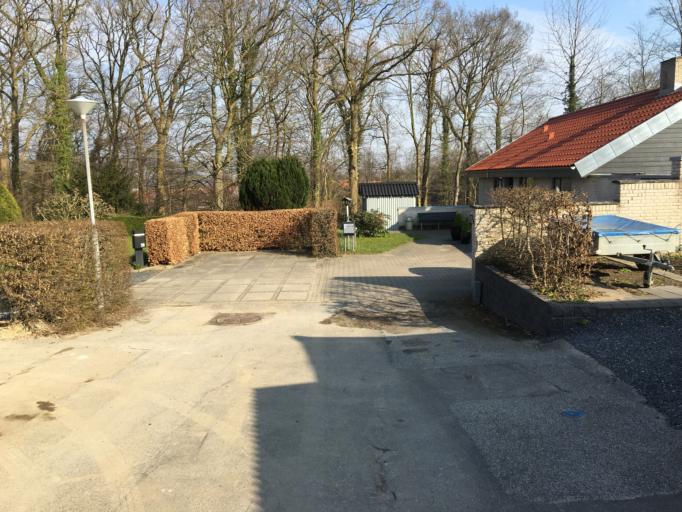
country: DK
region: South Denmark
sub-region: Middelfart Kommune
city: Middelfart
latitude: 55.5050
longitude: 9.7137
